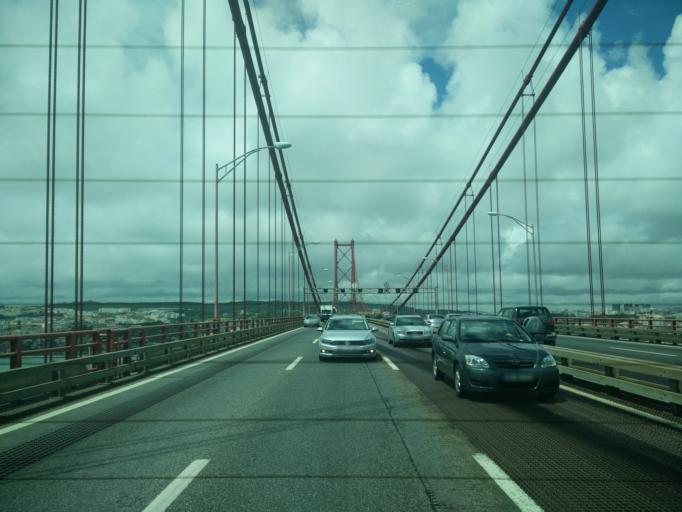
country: PT
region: Setubal
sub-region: Almada
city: Pragal
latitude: 38.6871
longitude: -9.1767
